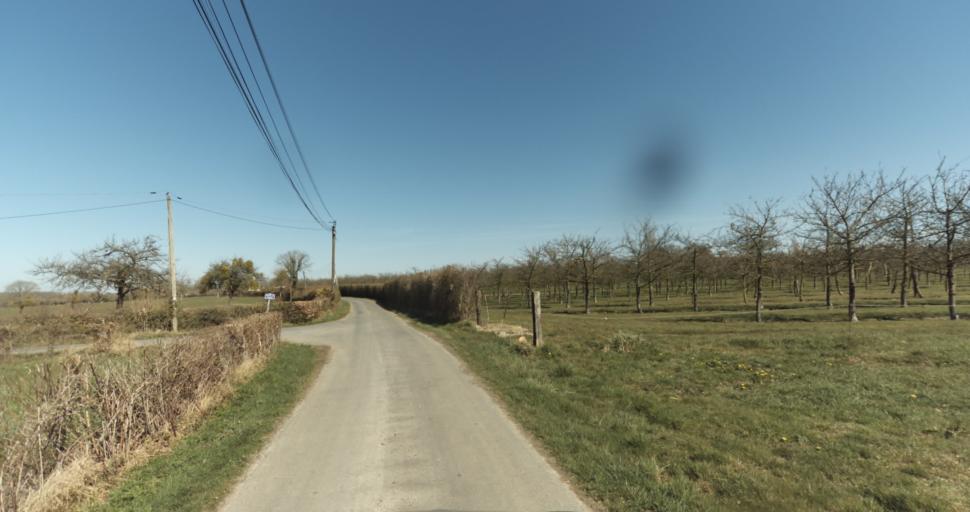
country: FR
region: Lower Normandy
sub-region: Departement du Calvados
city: Livarot
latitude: 49.0018
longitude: 0.1048
